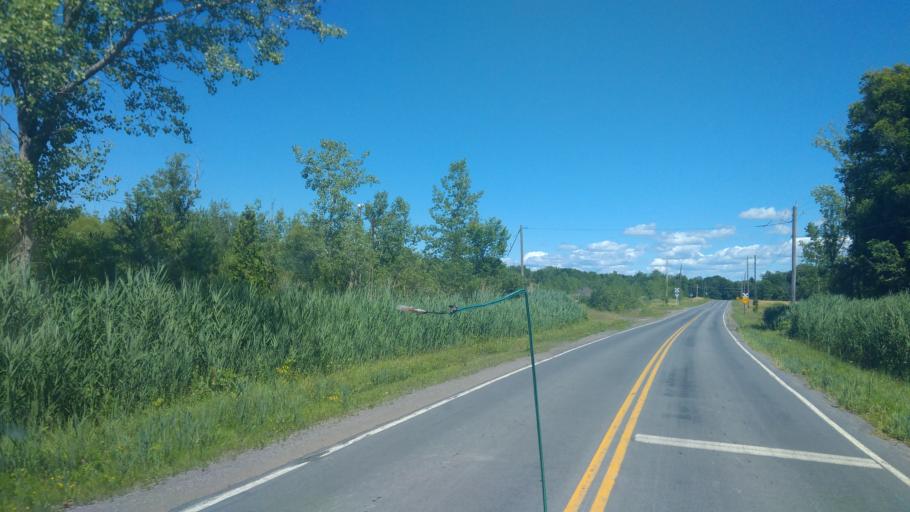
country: US
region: New York
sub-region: Wayne County
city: Sodus
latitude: 43.1833
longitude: -77.0377
